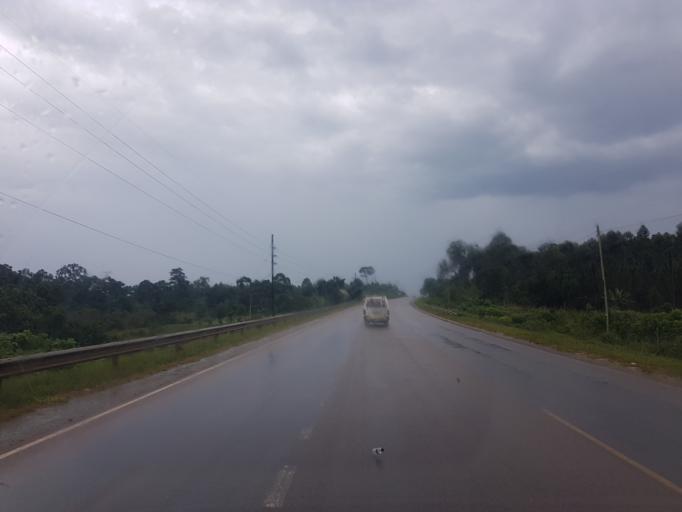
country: UG
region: Central Region
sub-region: Butambala District
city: Gombe
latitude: 0.0890
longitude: 32.1443
